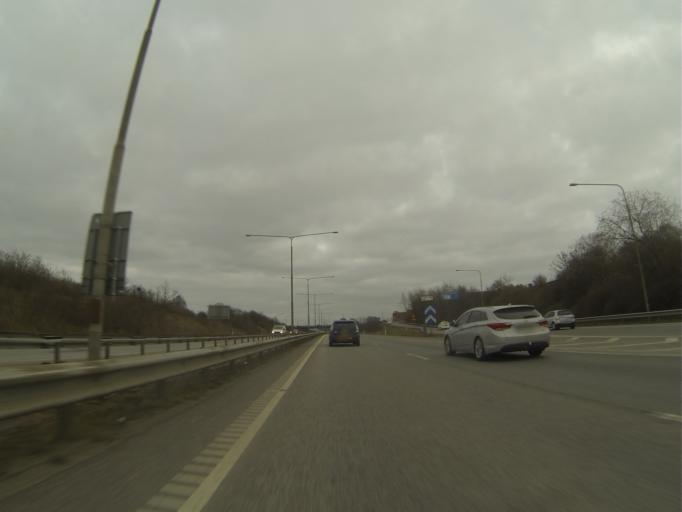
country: SE
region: Skane
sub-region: Malmo
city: Oxie
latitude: 55.5669
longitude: 13.0547
